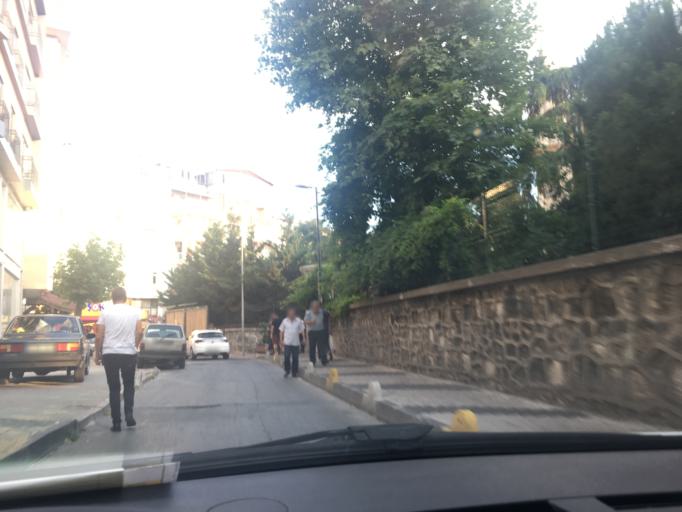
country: TR
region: Istanbul
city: Sisli
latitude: 41.0517
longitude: 28.9752
